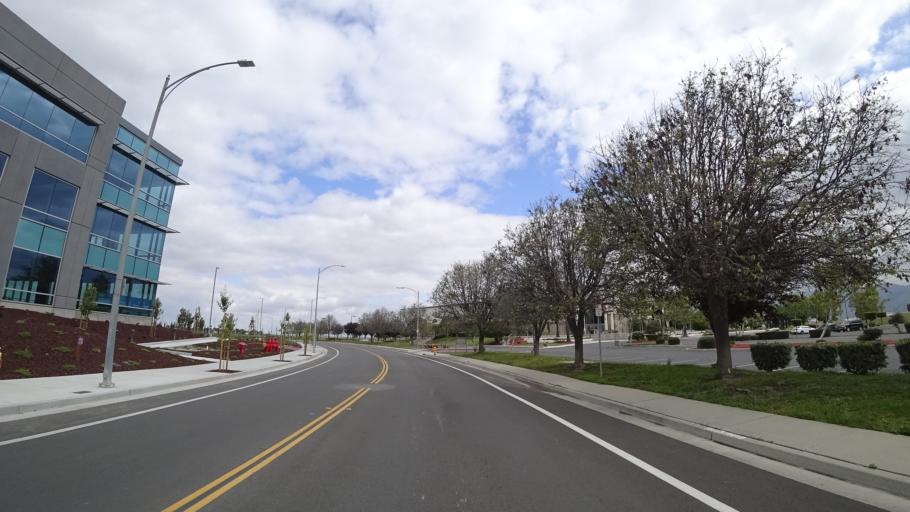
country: US
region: California
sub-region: Santa Clara County
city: Milpitas
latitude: 37.4244
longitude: -121.9605
